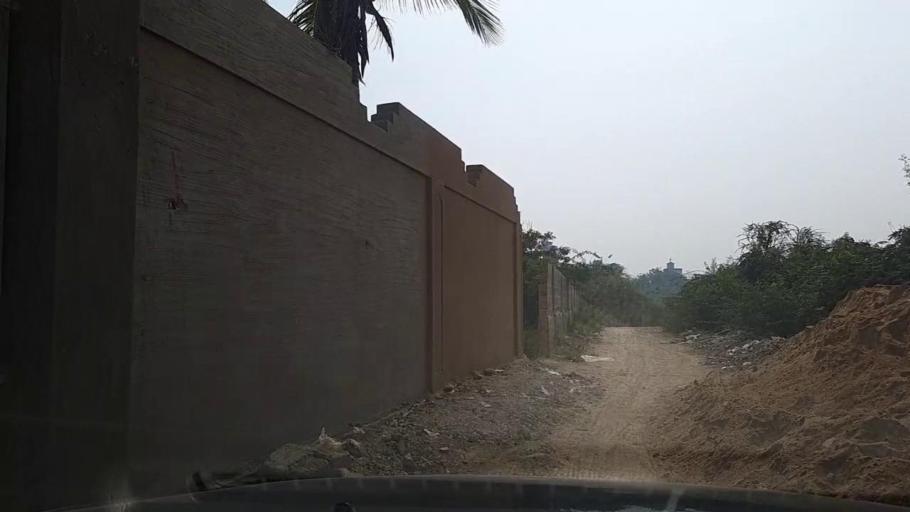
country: PK
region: Sindh
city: Thatta
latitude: 24.5537
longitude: 67.8395
